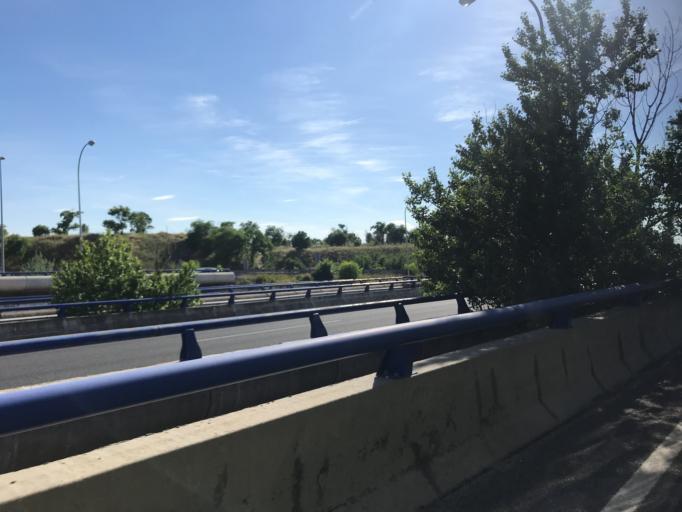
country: ES
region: Madrid
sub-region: Provincia de Madrid
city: Moratalaz
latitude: 40.4146
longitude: -3.6275
